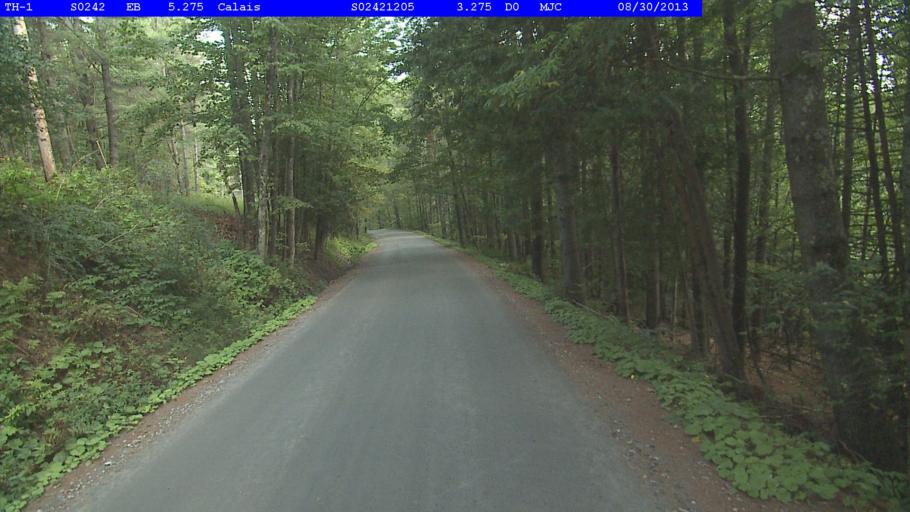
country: US
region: Vermont
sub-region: Washington County
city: Montpelier
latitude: 44.3672
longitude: -72.4813
